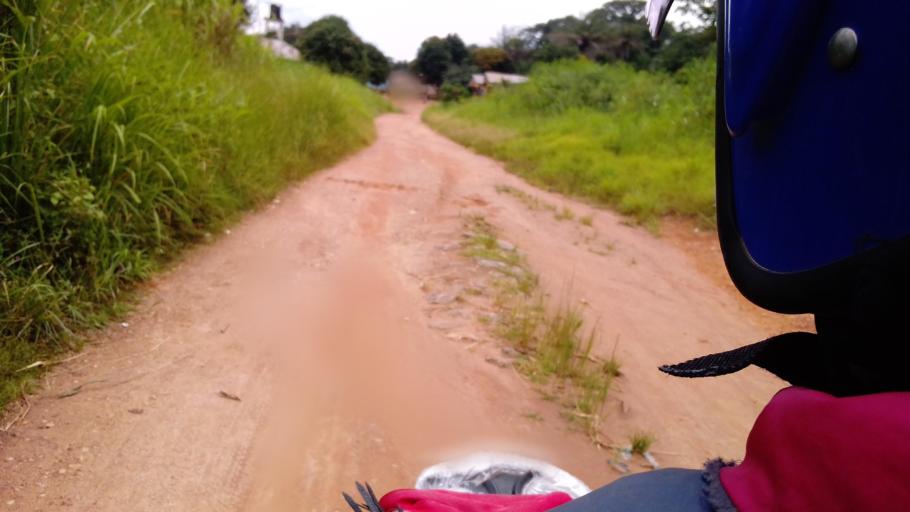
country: SL
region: Eastern Province
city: Koidu
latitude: 8.6675
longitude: -10.9471
